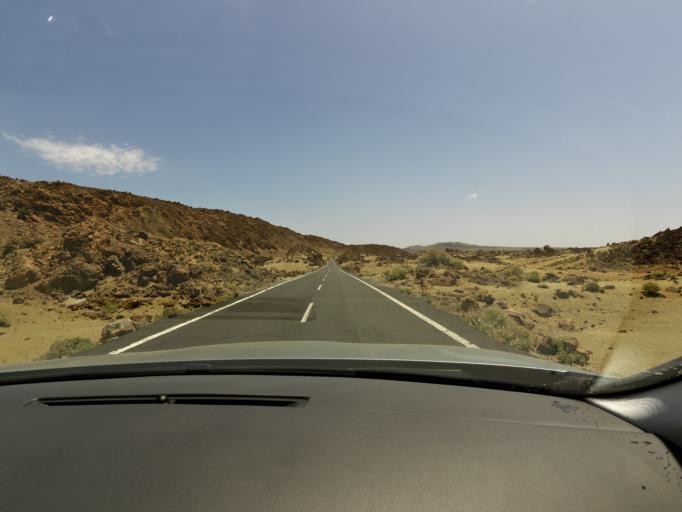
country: ES
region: Canary Islands
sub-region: Provincia de Santa Cruz de Tenerife
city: Los Realejos
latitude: 28.2662
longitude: -16.5880
